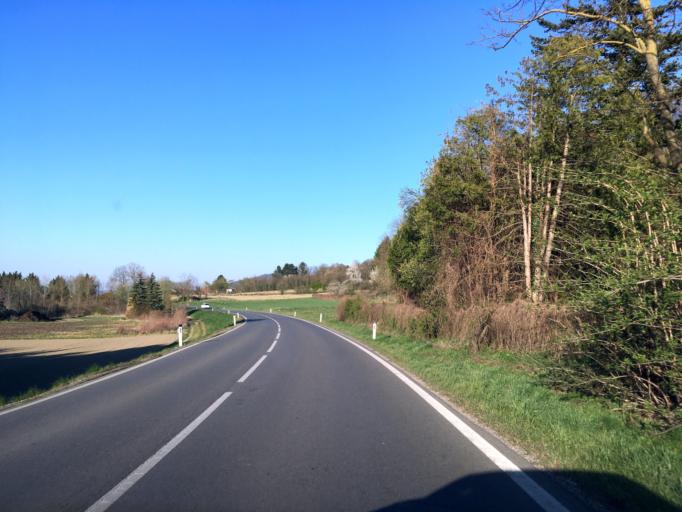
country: AT
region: Lower Austria
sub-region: Politischer Bezirk Tulln
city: Wordern
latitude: 48.3153
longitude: 16.1898
